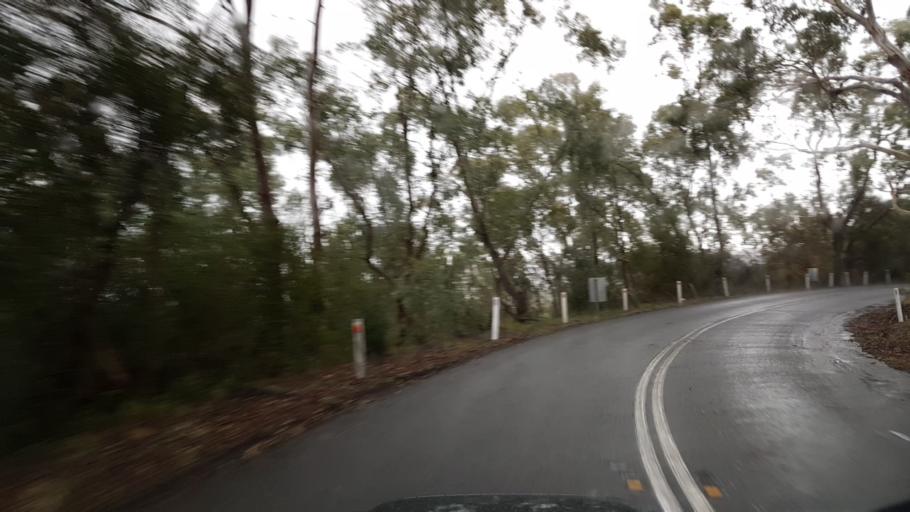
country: AU
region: South Australia
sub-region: Onkaparinga
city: Craigburn Farm
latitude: -35.0679
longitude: 138.6255
